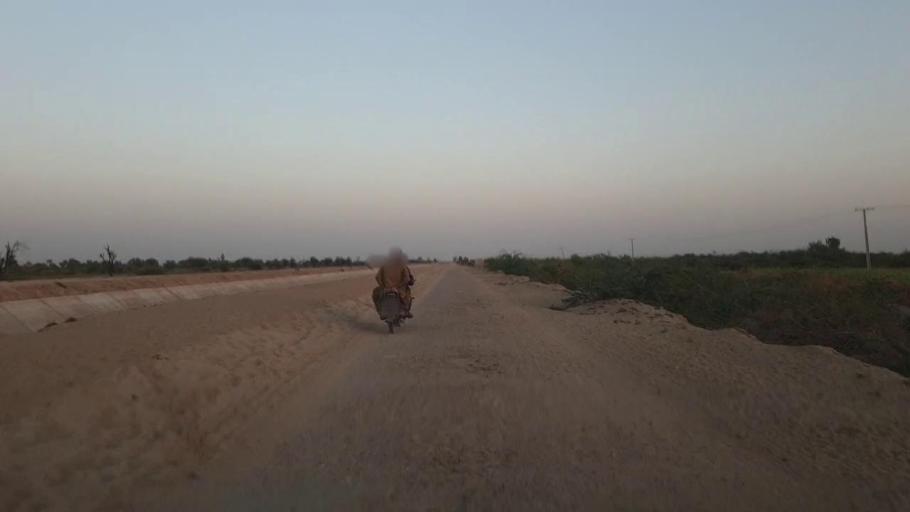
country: PK
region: Sindh
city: Dhoro Naro
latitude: 25.4372
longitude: 69.6421
